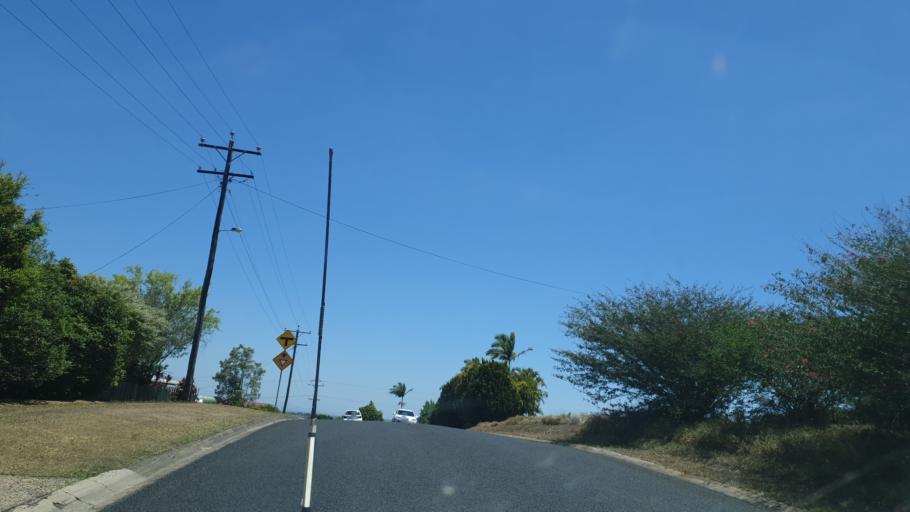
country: AU
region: Queensland
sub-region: Tablelands
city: Atherton
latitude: -17.2630
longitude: 145.4909
